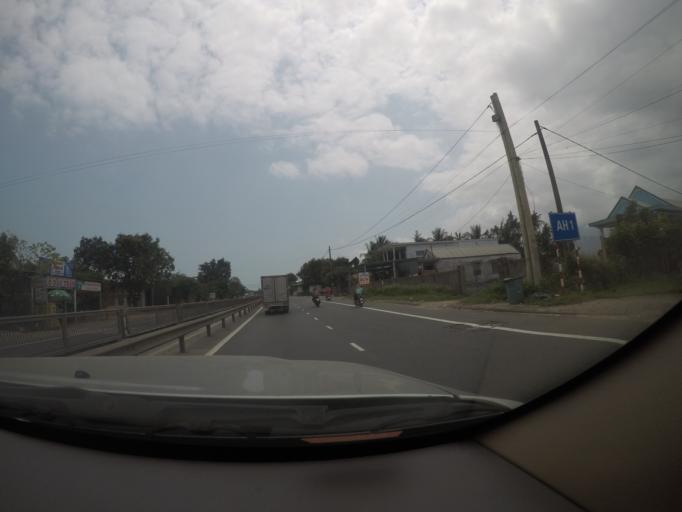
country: VN
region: Thua Thien-Hue
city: Phu Loc
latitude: 16.2642
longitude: 108.0502
